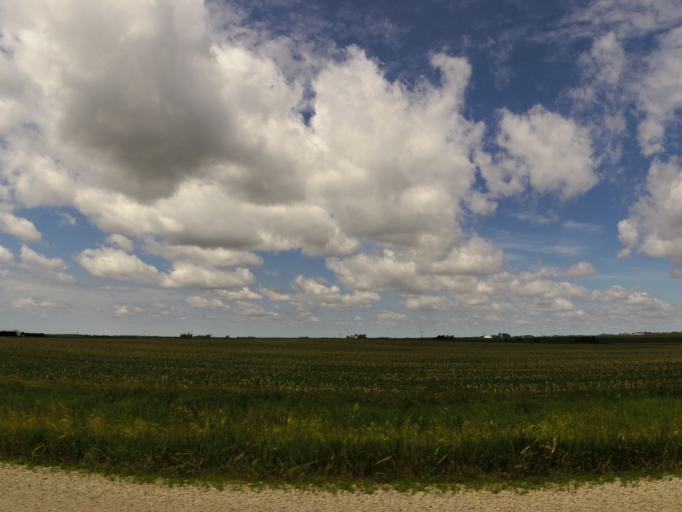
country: US
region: Iowa
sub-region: Chickasaw County
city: New Hampton
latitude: 43.1327
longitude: -92.2984
